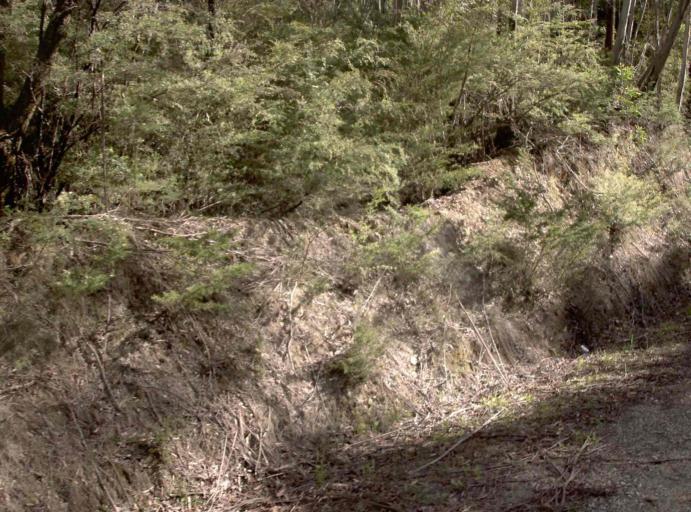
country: AU
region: Victoria
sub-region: East Gippsland
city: Lakes Entrance
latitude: -37.6665
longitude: 148.0690
